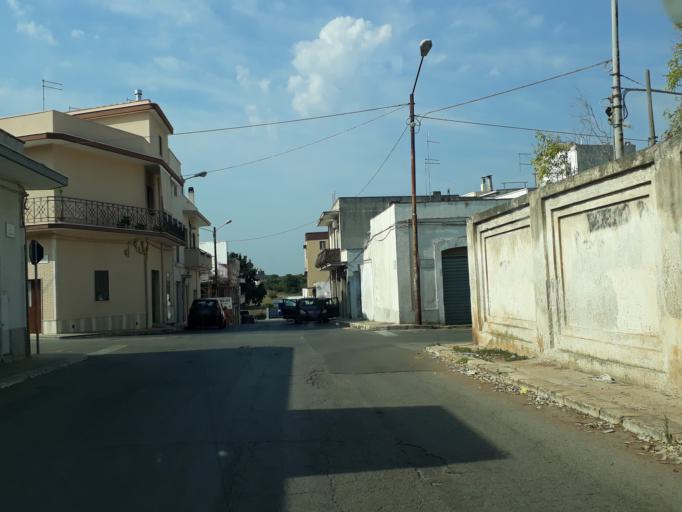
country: IT
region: Apulia
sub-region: Provincia di Brindisi
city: Carovigno
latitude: 40.7013
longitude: 17.6646
